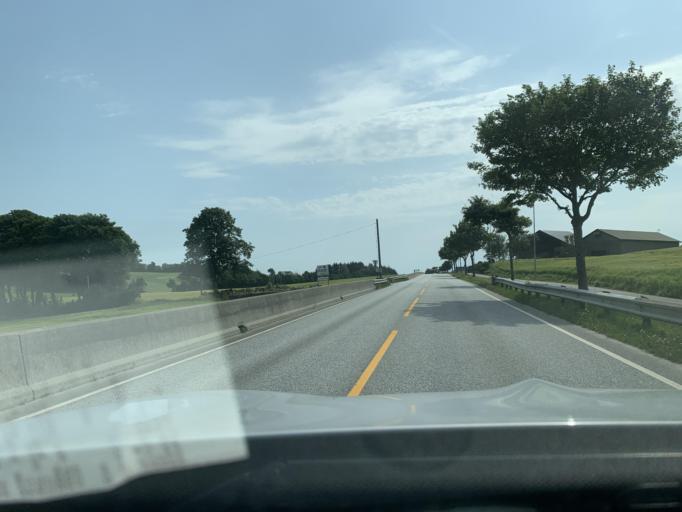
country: NO
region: Rogaland
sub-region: Klepp
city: Kleppe
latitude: 58.7649
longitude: 5.6264
